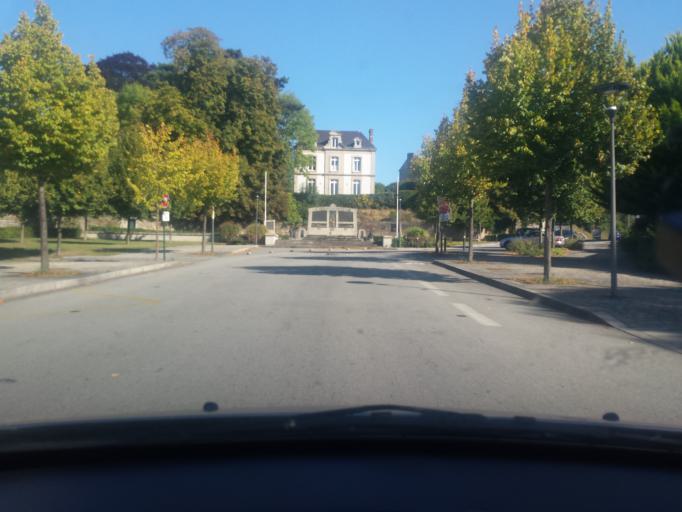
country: FR
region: Brittany
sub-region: Departement du Morbihan
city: Pontivy
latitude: 48.0645
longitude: -2.9622
